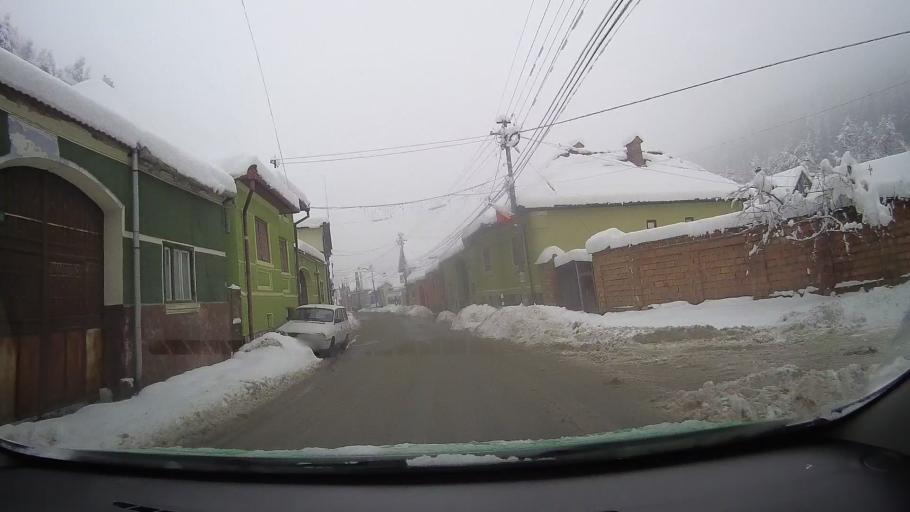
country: RO
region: Sibiu
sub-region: Comuna Tilisca
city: Tilisca
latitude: 45.8013
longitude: 23.8371
